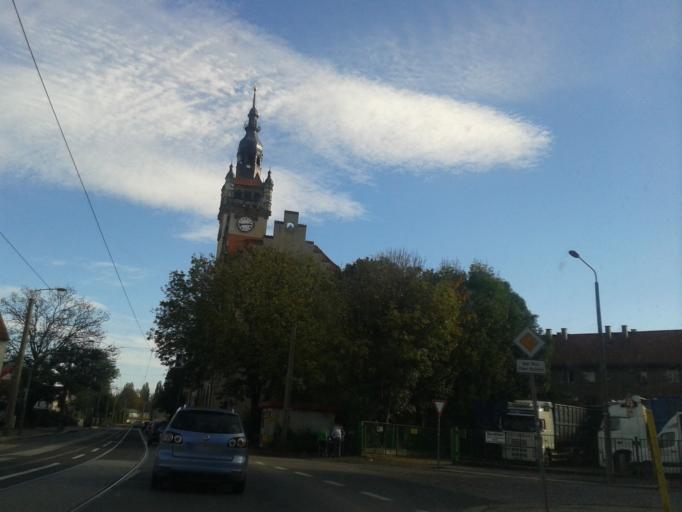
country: DE
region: Saxony
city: Dresden
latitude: 51.0569
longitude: 13.6870
